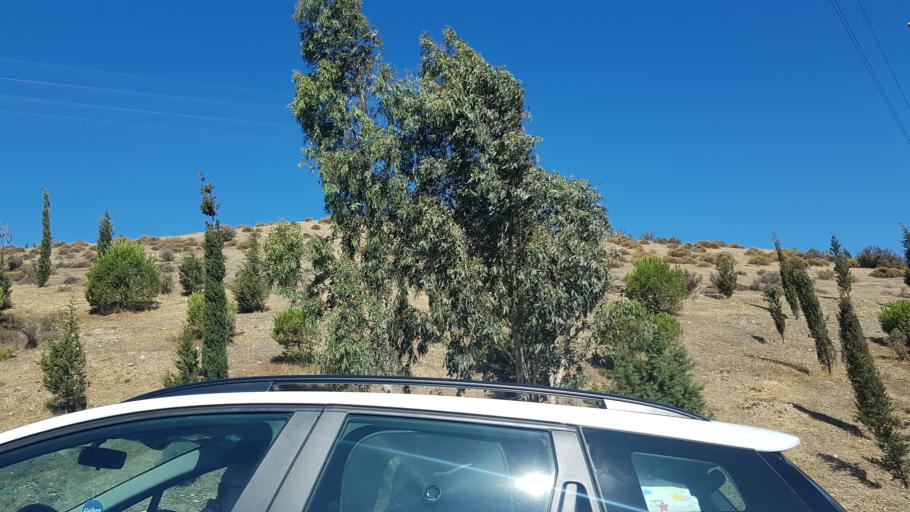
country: TR
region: Izmir
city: Buca
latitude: 38.4073
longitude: 27.2342
